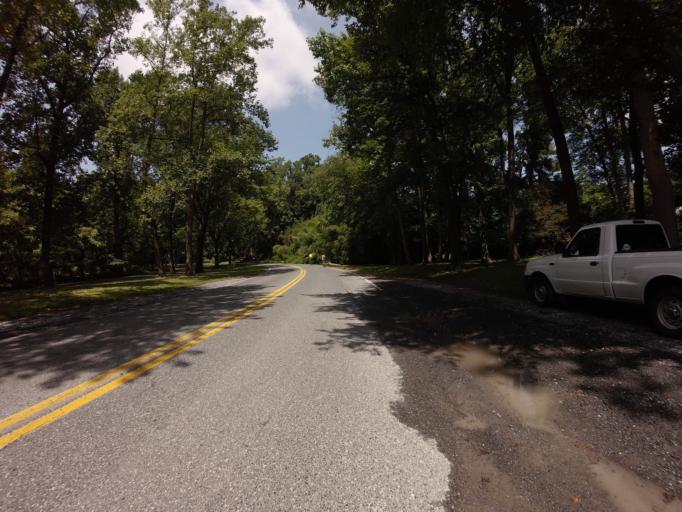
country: US
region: Maryland
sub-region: Montgomery County
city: South Kensington
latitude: 39.0085
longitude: -77.0823
